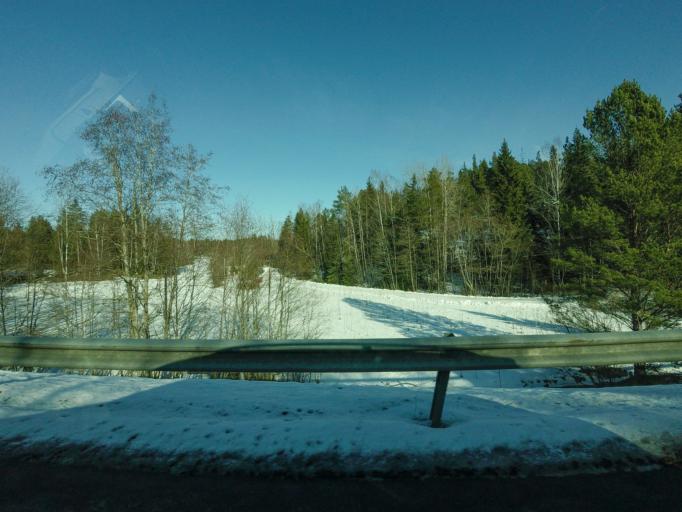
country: FI
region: Uusimaa
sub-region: Raaseporin
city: Inga
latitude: 60.1019
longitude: 23.9061
